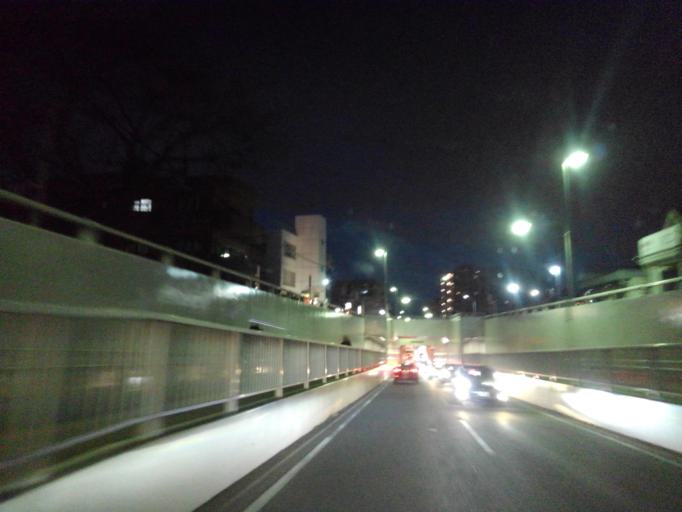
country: JP
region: Saitama
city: Tokorozawa
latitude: 35.8033
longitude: 139.4582
